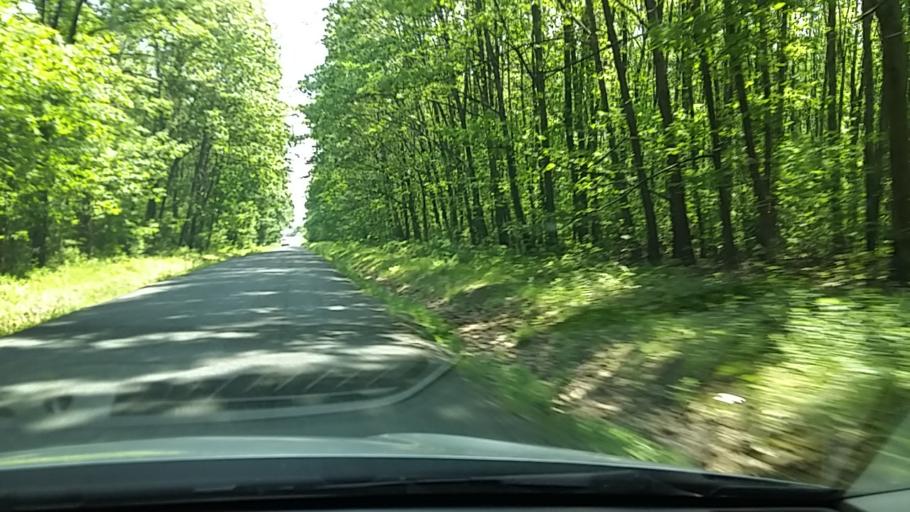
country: HU
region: Vas
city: Kormend
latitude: 46.9660
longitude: 16.5848
